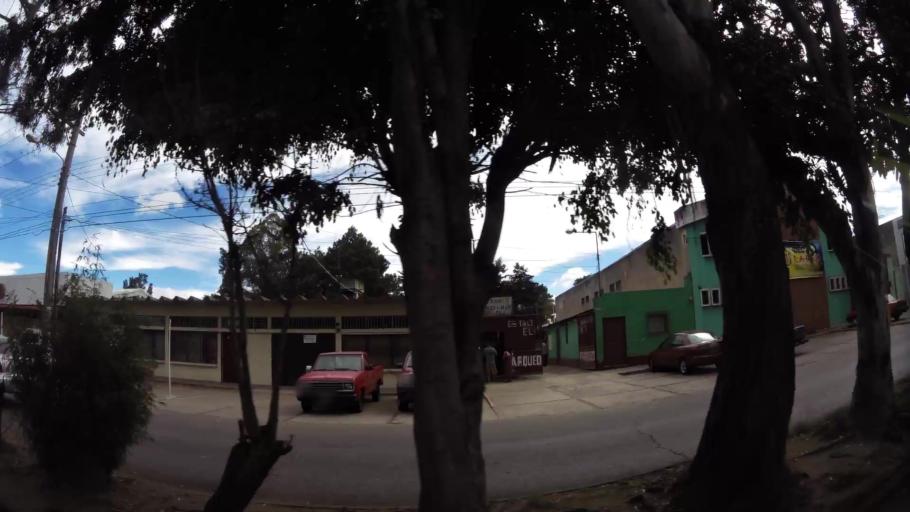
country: GT
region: Guatemala
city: Mixco
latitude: 14.6636
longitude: -90.5704
